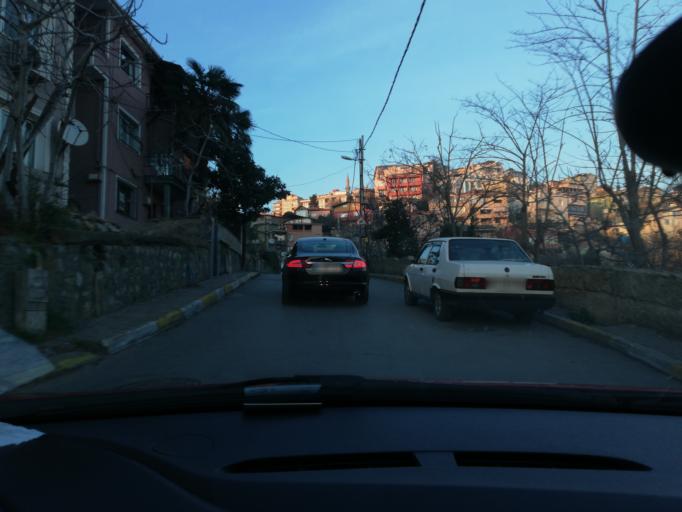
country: TR
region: Istanbul
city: UEskuedar
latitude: 41.0819
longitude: 29.0766
